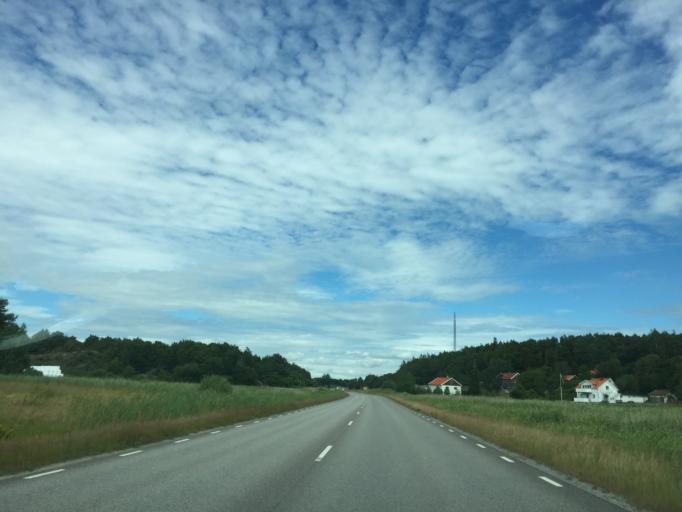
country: SE
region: Vaestra Goetaland
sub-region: Tjorns Kommun
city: Skaerhamn
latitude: 58.0061
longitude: 11.6096
